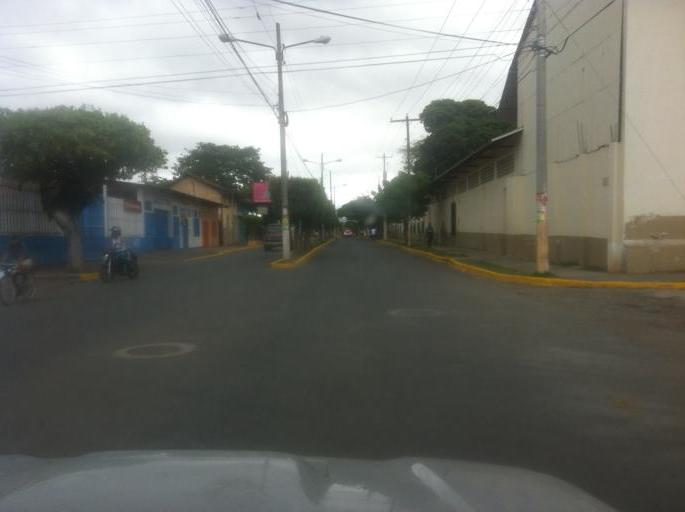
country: NI
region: Granada
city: Granada
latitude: 11.9367
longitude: -85.9568
